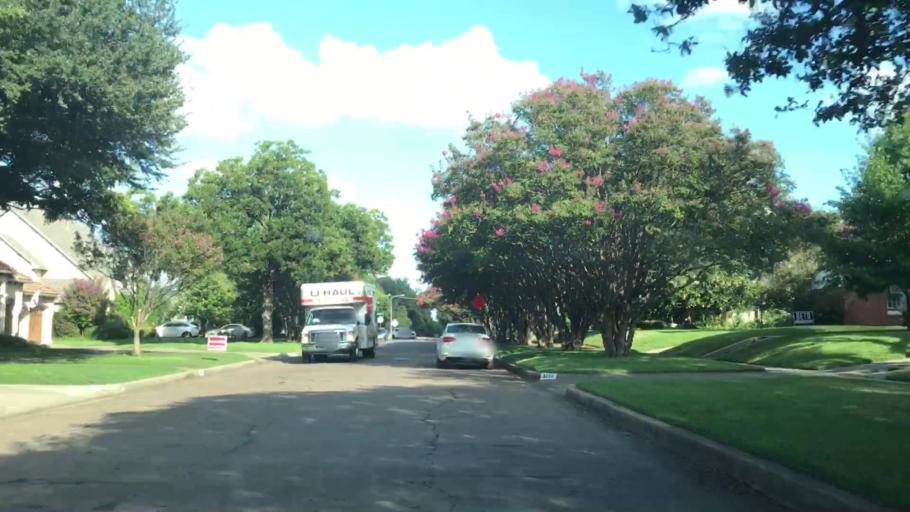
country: US
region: Texas
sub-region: Dallas County
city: Highland Park
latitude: 32.8293
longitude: -96.7542
